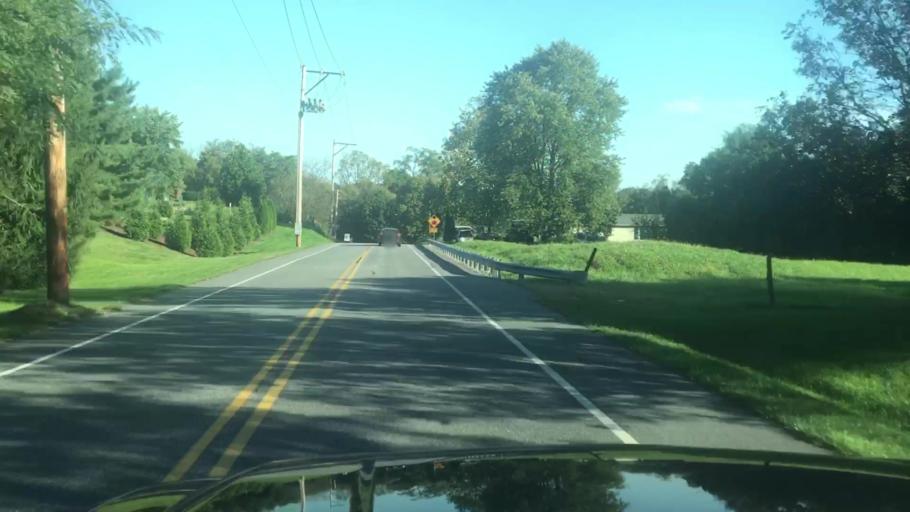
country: US
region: Pennsylvania
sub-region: Cumberland County
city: Shiremanstown
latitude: 40.2669
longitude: -76.9868
